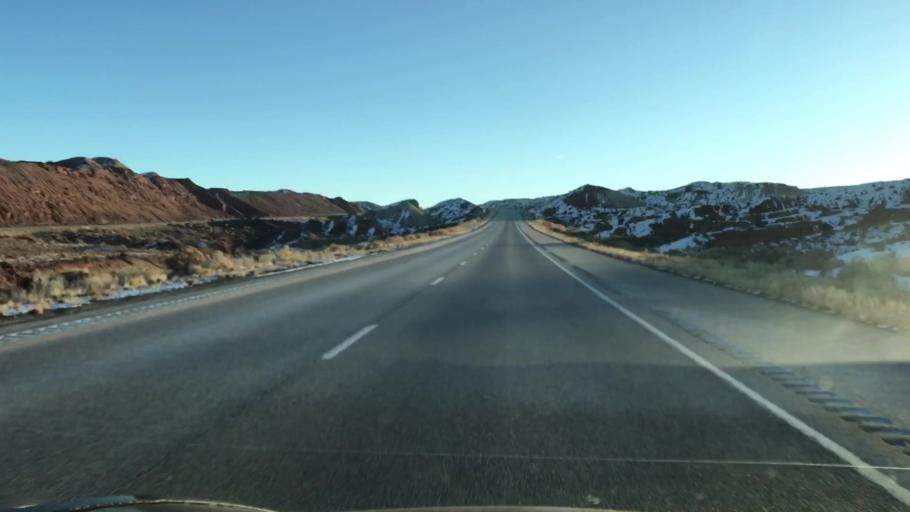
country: US
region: Utah
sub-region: Emery County
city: Ferron
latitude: 38.8467
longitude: -111.0316
